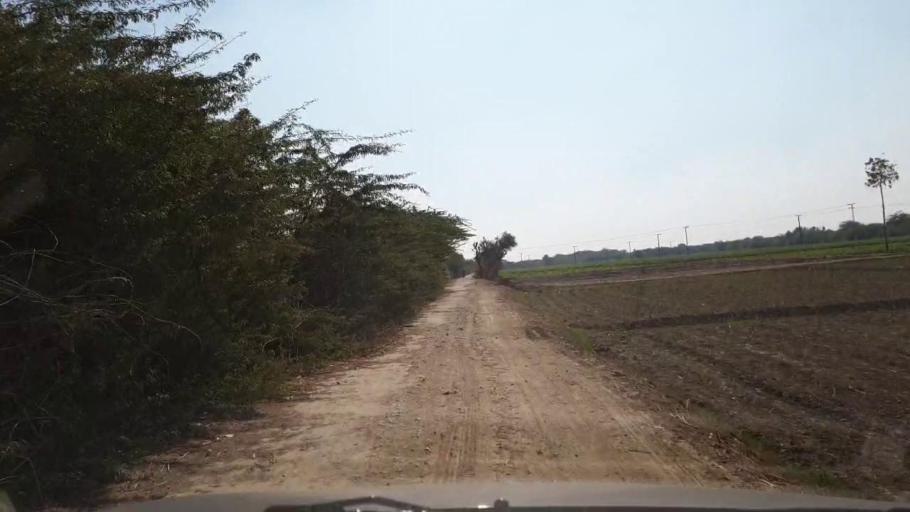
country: PK
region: Sindh
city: Jhol
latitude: 25.8933
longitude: 68.8291
